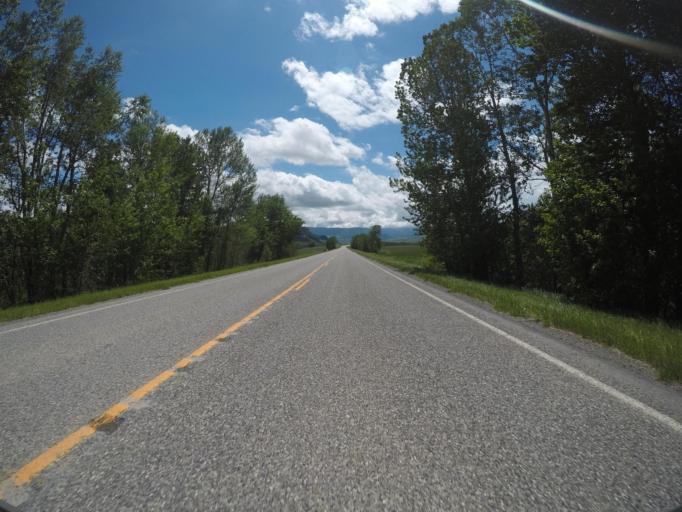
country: US
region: Montana
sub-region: Sweet Grass County
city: Big Timber
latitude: 45.6525
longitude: -110.1142
